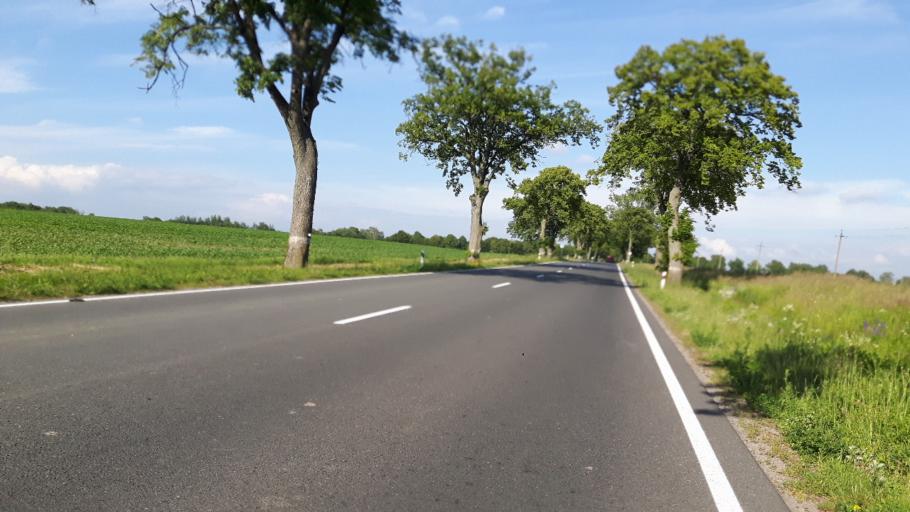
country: RU
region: Kaliningrad
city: Mamonovo
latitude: 54.4858
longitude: 20.0352
